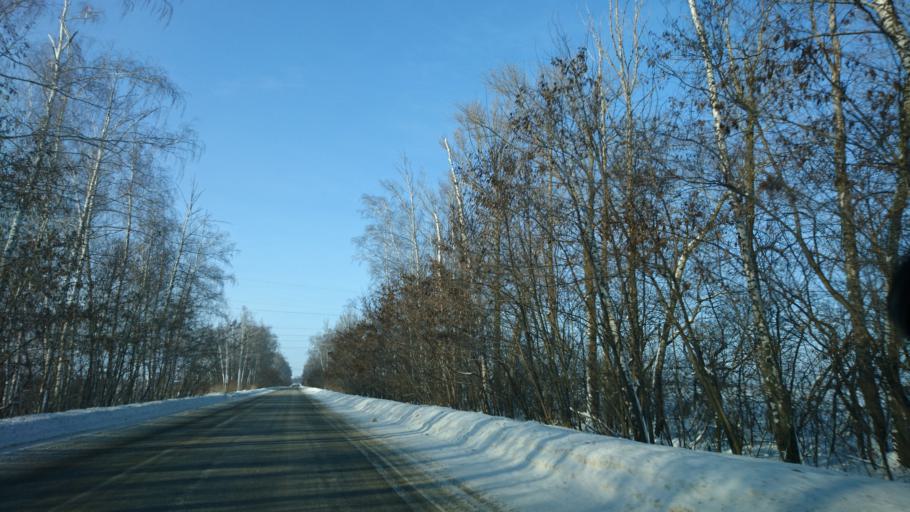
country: RU
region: Belgorod
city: Severnyy
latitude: 50.7287
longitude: 36.5429
